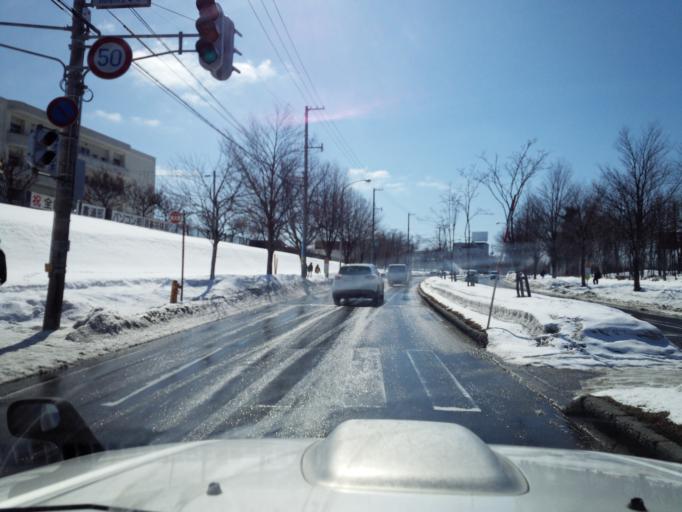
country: JP
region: Hokkaido
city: Kitahiroshima
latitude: 42.9982
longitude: 141.4609
